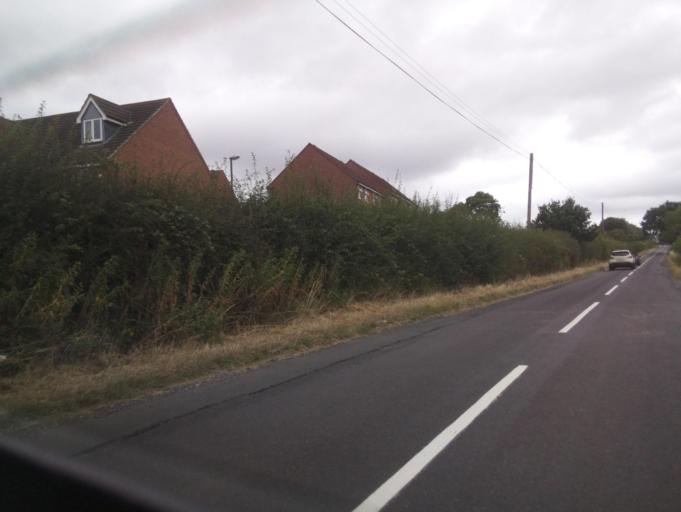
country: GB
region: England
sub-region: Derbyshire
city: Findern
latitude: 52.8912
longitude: -1.5164
